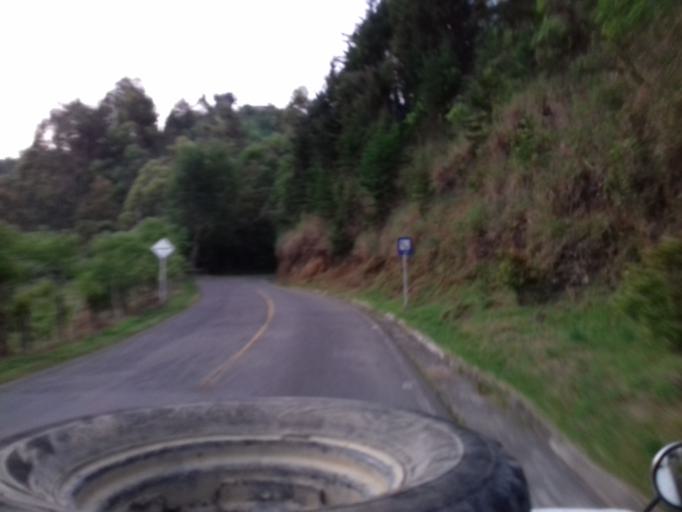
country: CO
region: Quindio
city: Salento
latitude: 4.6434
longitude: -75.5747
